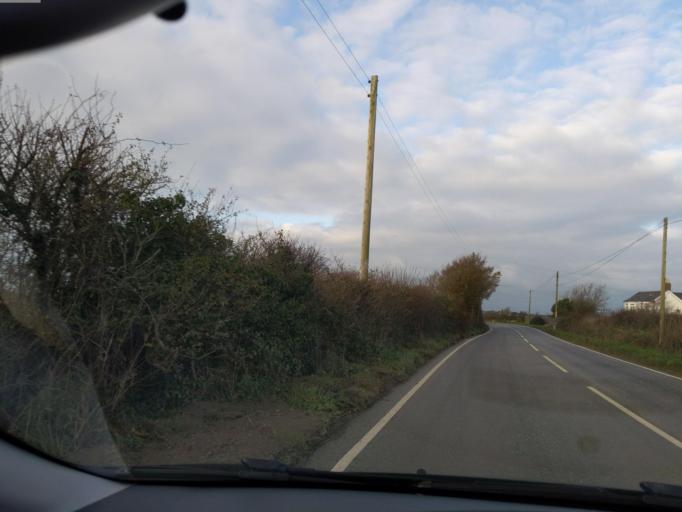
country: GB
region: England
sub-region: Cornwall
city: Padstow
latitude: 50.5163
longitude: -4.9500
